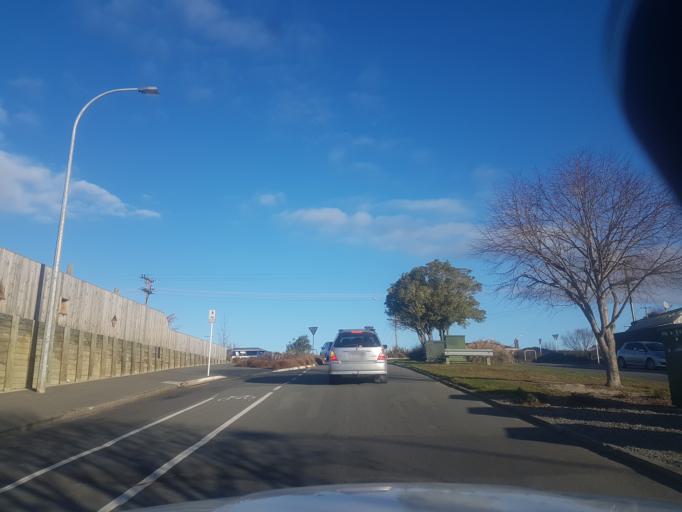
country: NZ
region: Canterbury
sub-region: Timaru District
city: Timaru
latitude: -44.3882
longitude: 171.2098
